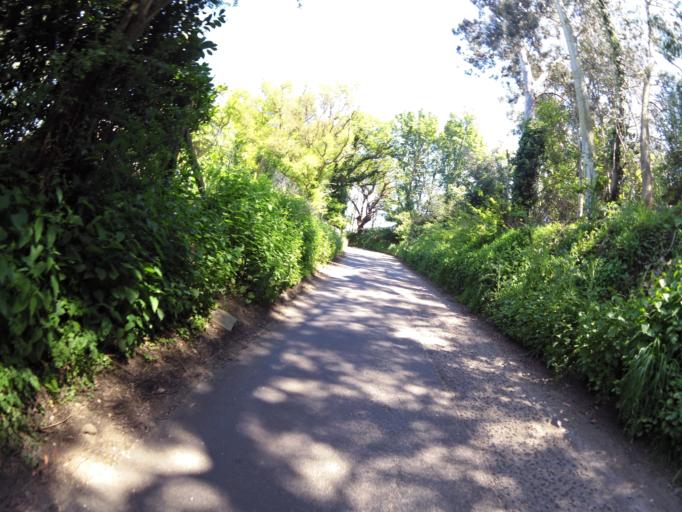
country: GB
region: England
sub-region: Suffolk
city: Ipswich
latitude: 51.9794
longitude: 1.1638
